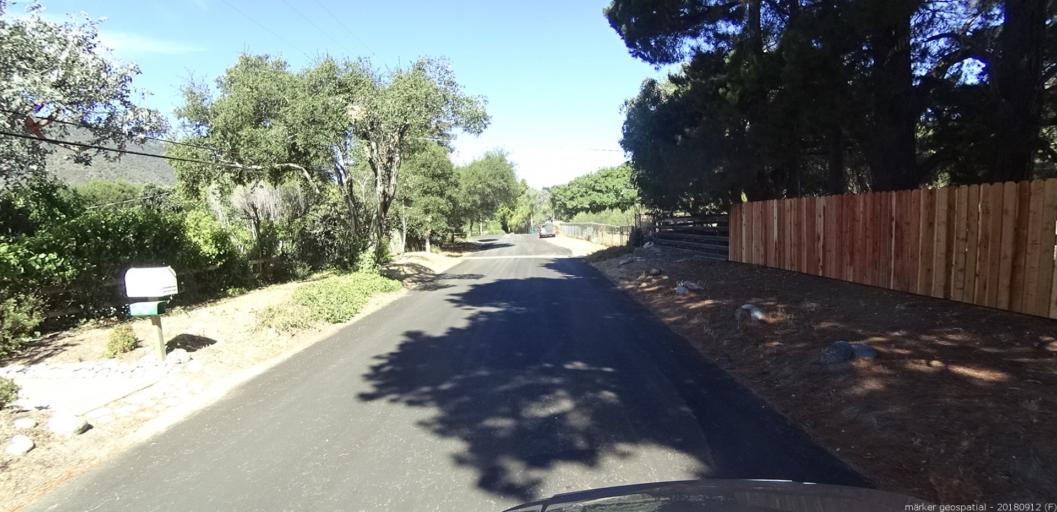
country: US
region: California
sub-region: Monterey County
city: Carmel Valley Village
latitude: 36.4880
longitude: -121.7450
